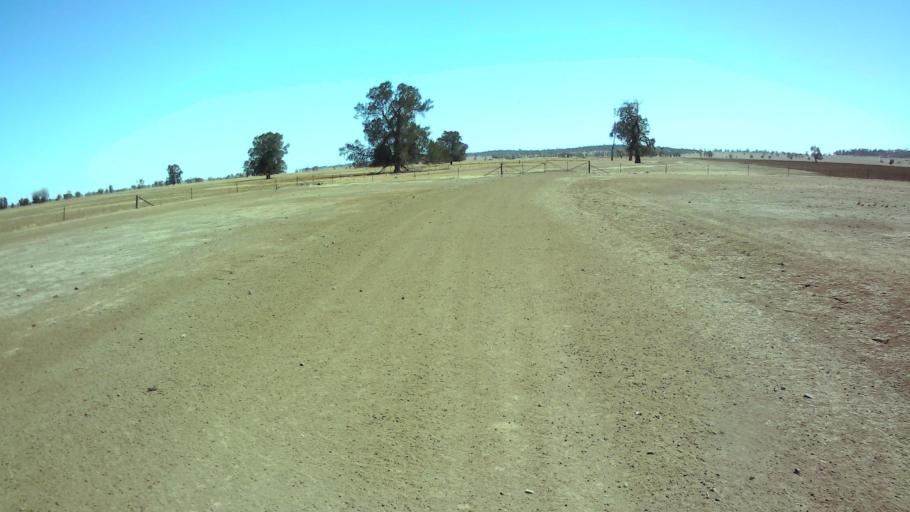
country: AU
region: New South Wales
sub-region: Forbes
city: Forbes
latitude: -33.7126
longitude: 147.6671
